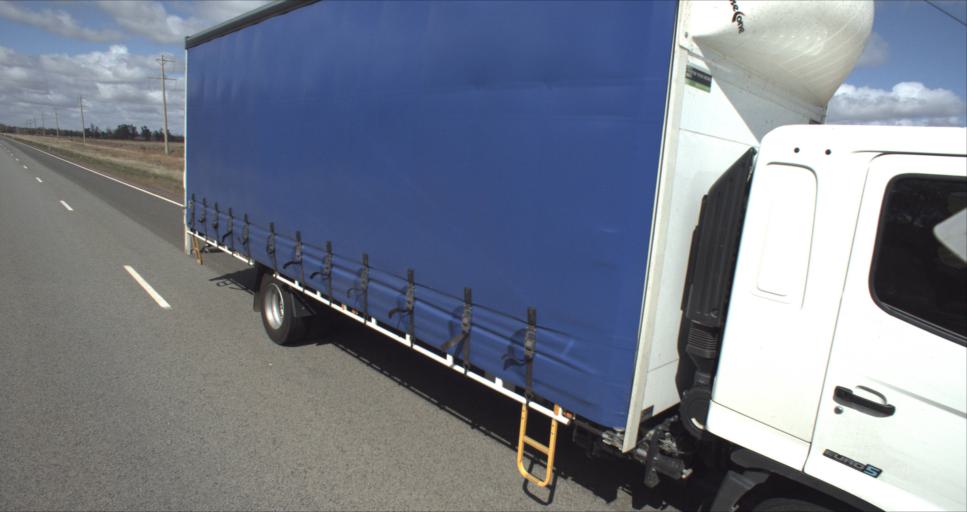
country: AU
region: New South Wales
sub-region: Murrumbidgee Shire
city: Darlington Point
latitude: -34.5834
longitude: 146.1647
